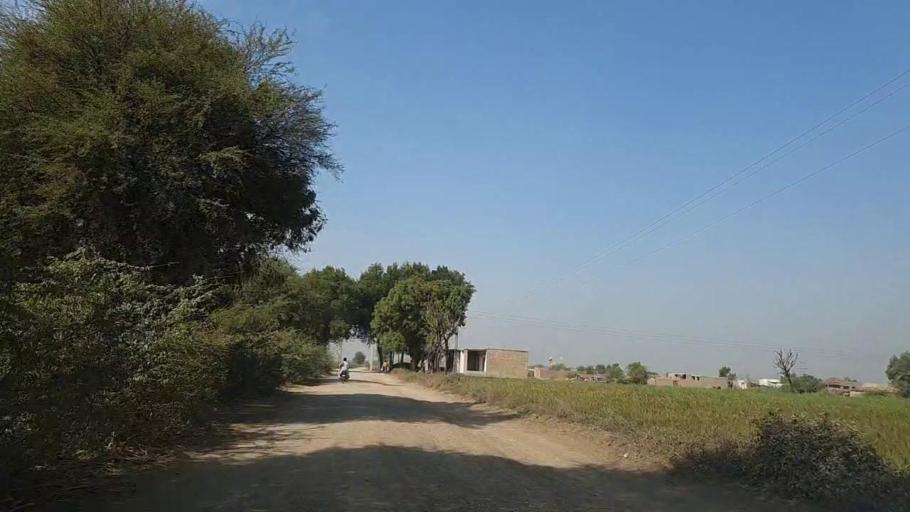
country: PK
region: Sindh
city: Mirpur Khas
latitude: 25.4824
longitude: 69.0089
